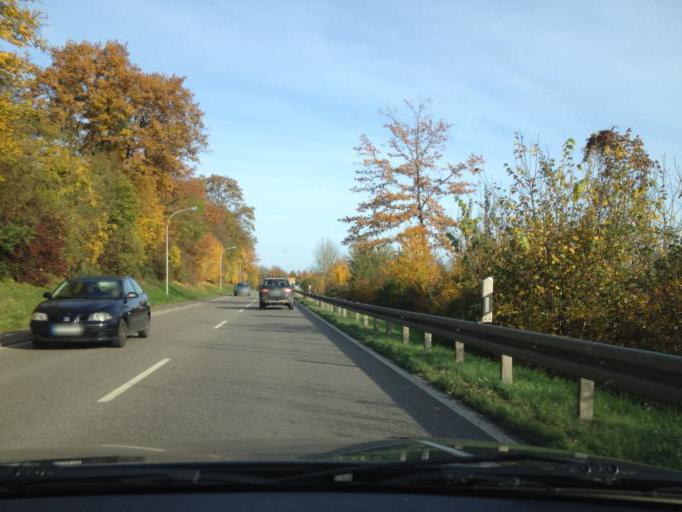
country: DE
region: Baden-Wuerttemberg
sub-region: Regierungsbezirk Stuttgart
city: Neckarsulm
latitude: 49.2081
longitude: 9.2450
